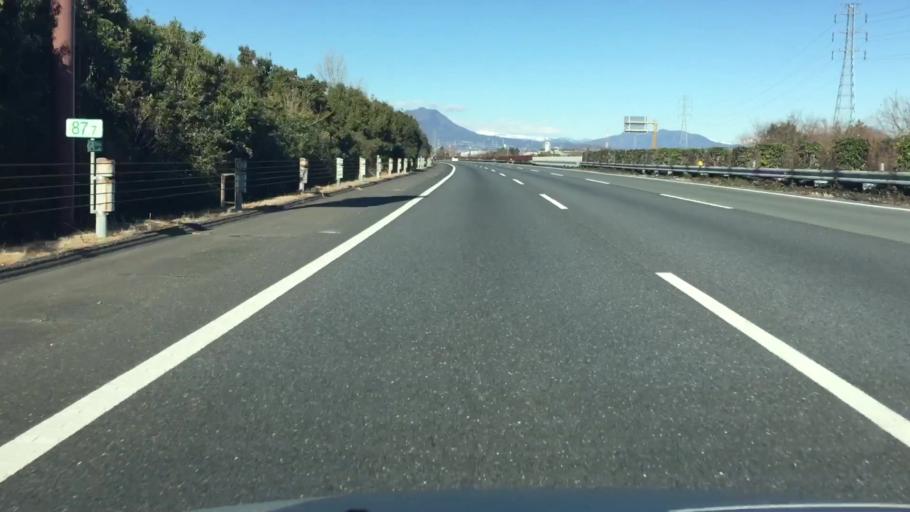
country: JP
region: Gunma
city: Takasaki
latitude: 36.3423
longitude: 139.0558
